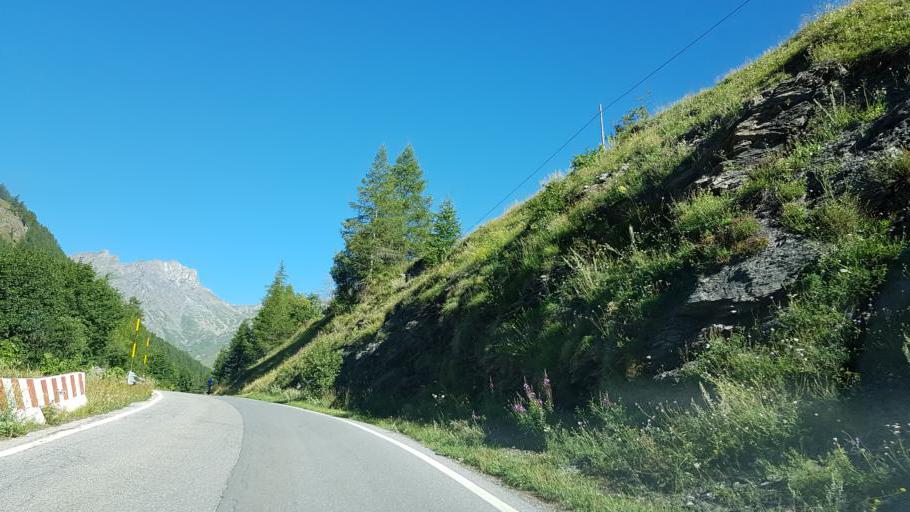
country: IT
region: Piedmont
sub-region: Provincia di Cuneo
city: Pontechianale
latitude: 44.6283
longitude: 7.0215
